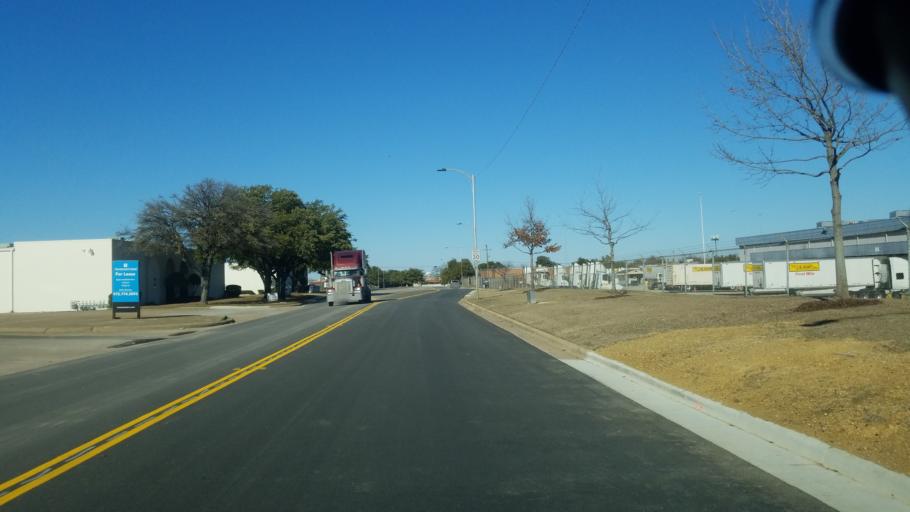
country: US
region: Texas
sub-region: Tarrant County
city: Arlington
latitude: 32.7534
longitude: -97.0542
